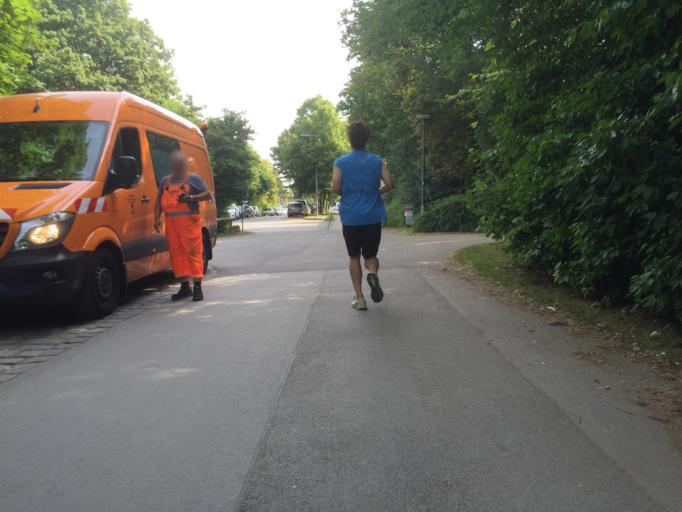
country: DE
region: Bavaria
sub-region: Upper Bavaria
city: Neubiberg
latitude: 48.1156
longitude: 11.6388
